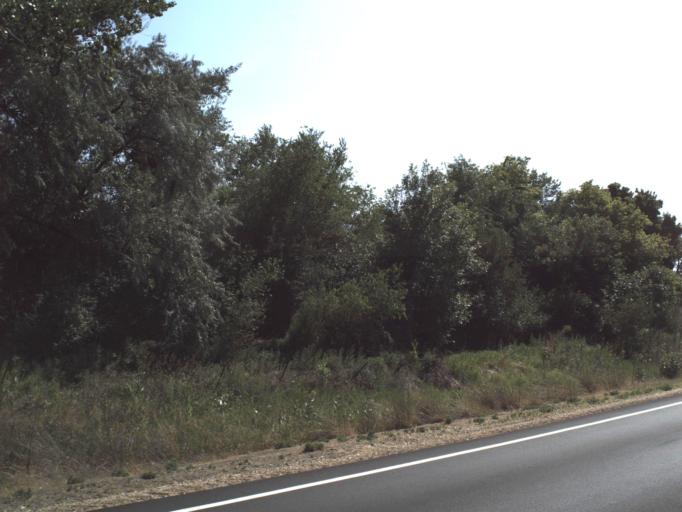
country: US
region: Utah
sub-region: Weber County
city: Marriott-Slaterville
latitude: 41.2451
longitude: -112.0361
